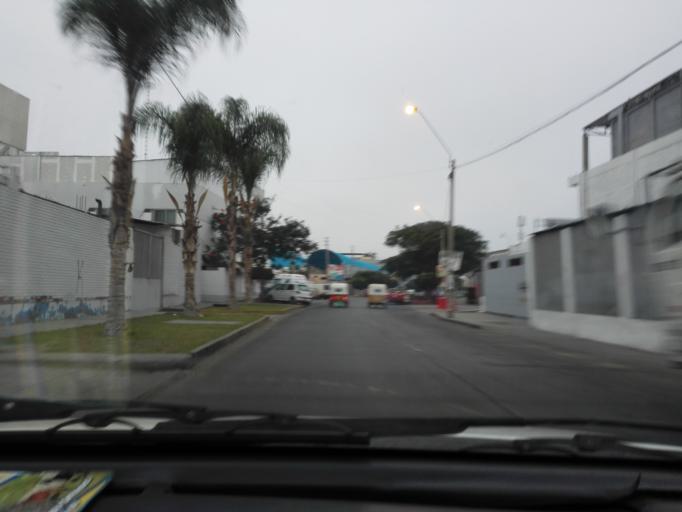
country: PE
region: Ica
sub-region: Provincia de Ica
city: Ica
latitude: -14.0709
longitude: -75.7273
